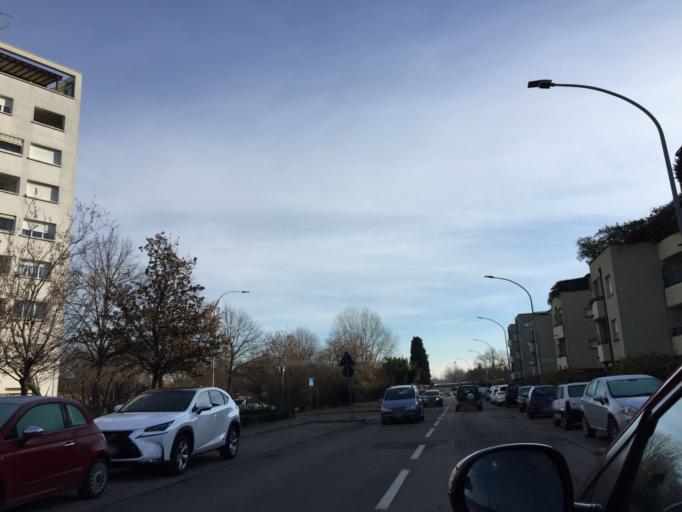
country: IT
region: Emilia-Romagna
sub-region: Provincia di Bologna
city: Casalecchio di Reno
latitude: 44.4997
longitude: 11.2996
